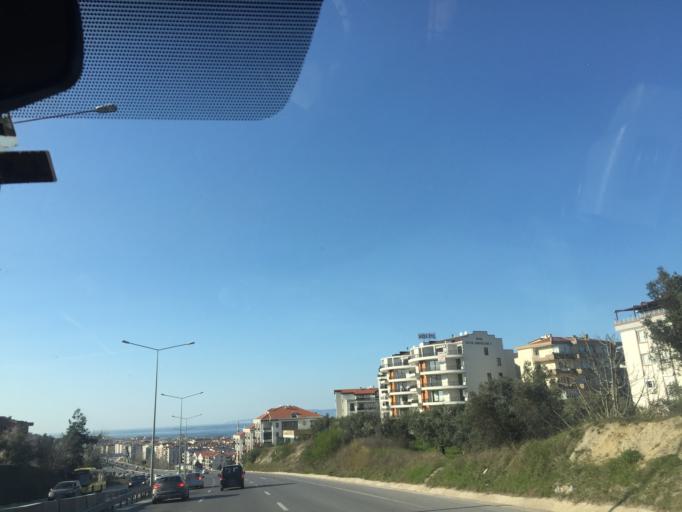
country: TR
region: Bursa
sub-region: Mudanya
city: Mudanya
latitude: 40.3516
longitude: 28.9210
